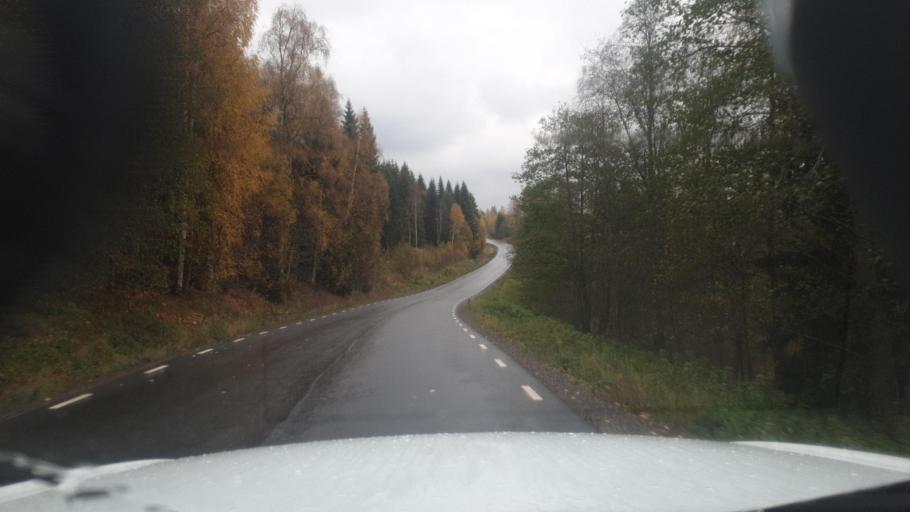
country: SE
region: Vaermland
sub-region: Torsby Kommun
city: Torsby
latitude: 59.9809
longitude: 12.8185
